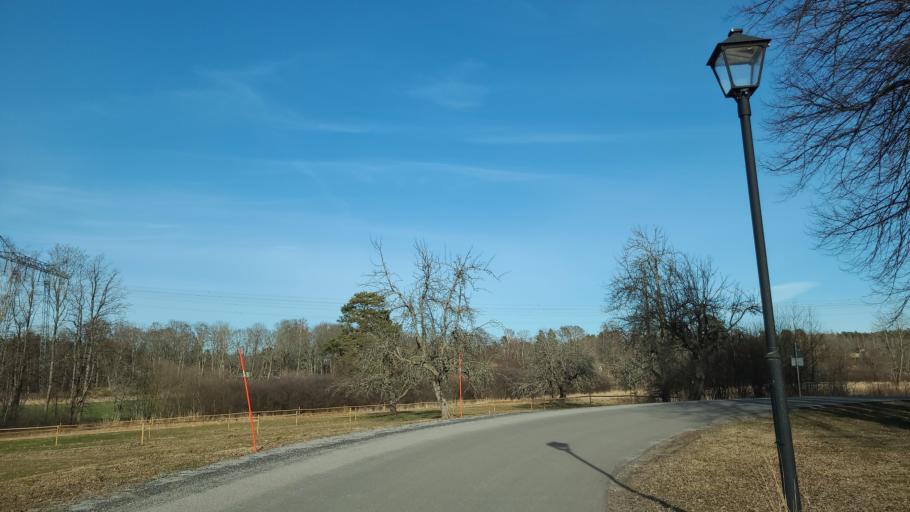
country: SE
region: Stockholm
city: Stenhamra
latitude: 59.2847
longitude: 17.6611
